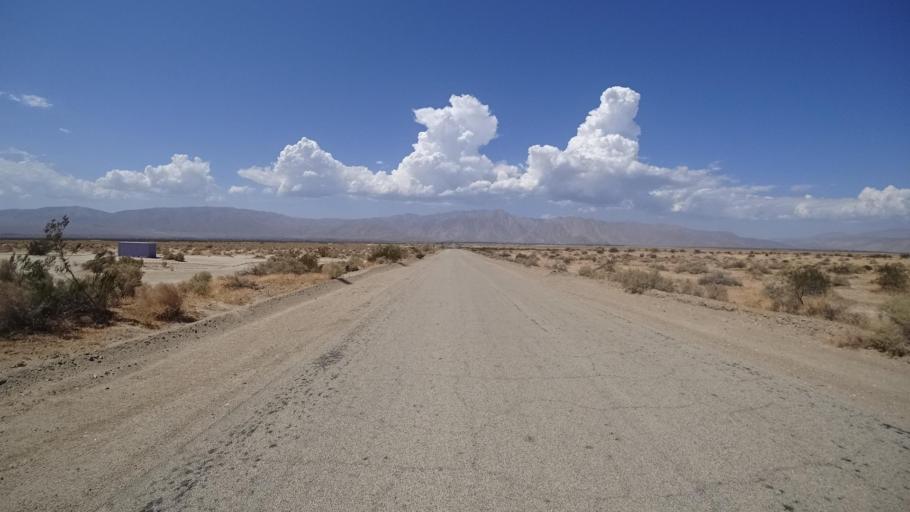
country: US
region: California
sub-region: San Diego County
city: Borrego Springs
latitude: 33.2577
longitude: -116.2958
